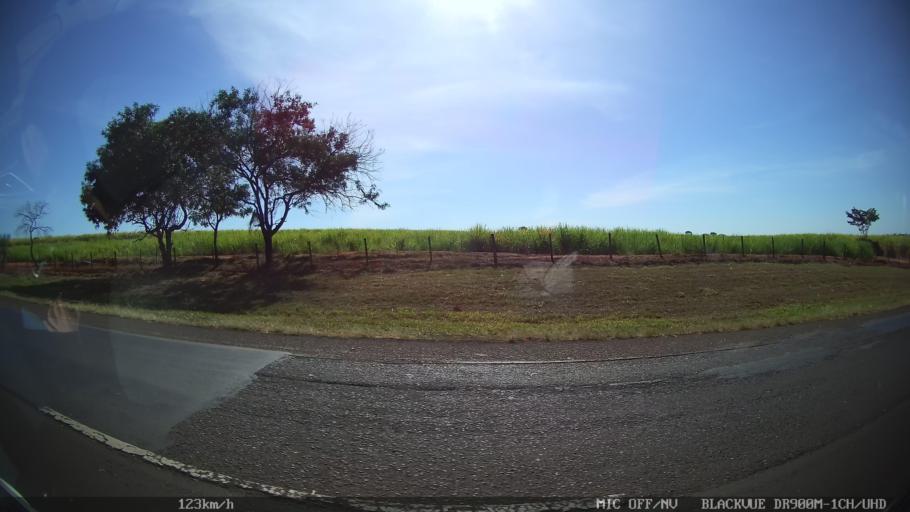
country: BR
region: Sao Paulo
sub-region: Barretos
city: Barretos
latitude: -20.5631
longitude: -48.6567
